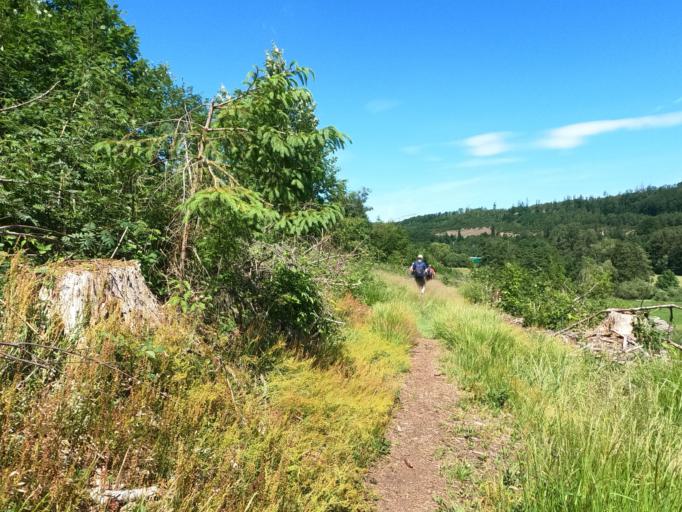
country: DE
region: Rheinland-Pfalz
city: Alpenrod
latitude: 50.6613
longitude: 7.8769
